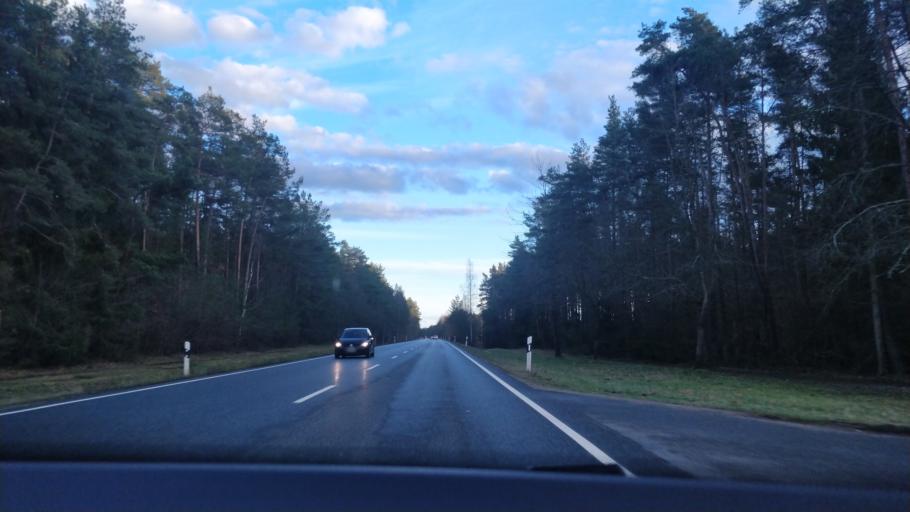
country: DE
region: Bavaria
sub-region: Upper Palatinate
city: Pressath
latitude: 49.7485
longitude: 11.9379
